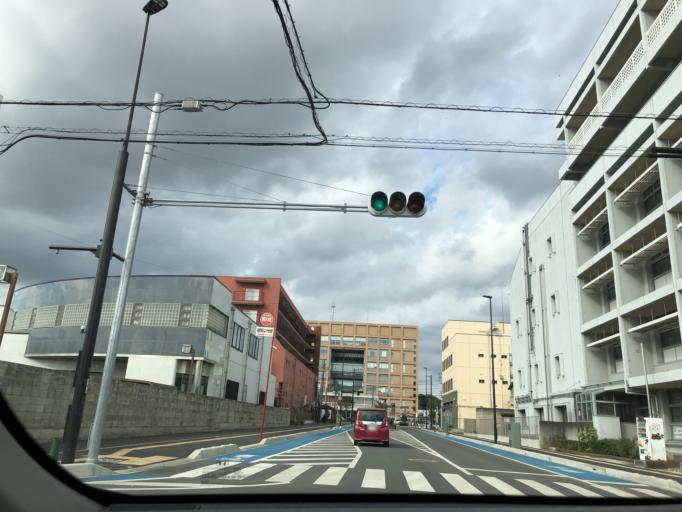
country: JP
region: Tochigi
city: Sano
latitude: 36.3122
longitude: 139.5784
